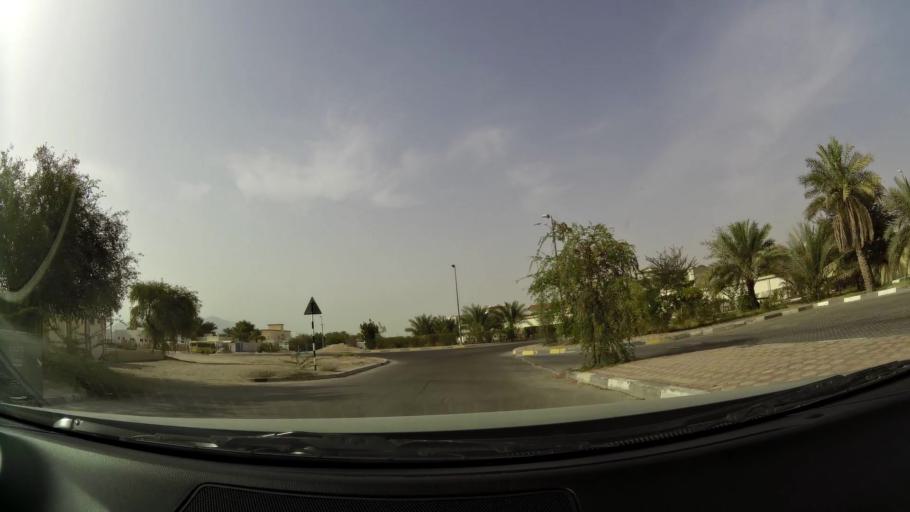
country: AE
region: Abu Dhabi
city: Al Ain
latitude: 24.1421
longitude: 55.7074
